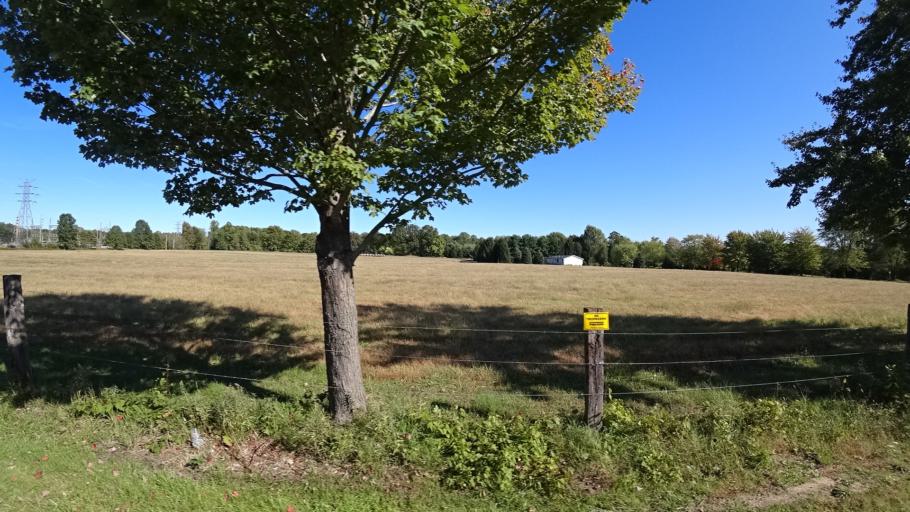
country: US
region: Indiana
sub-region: LaPorte County
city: Trail Creek
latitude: 41.7101
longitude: -86.8405
